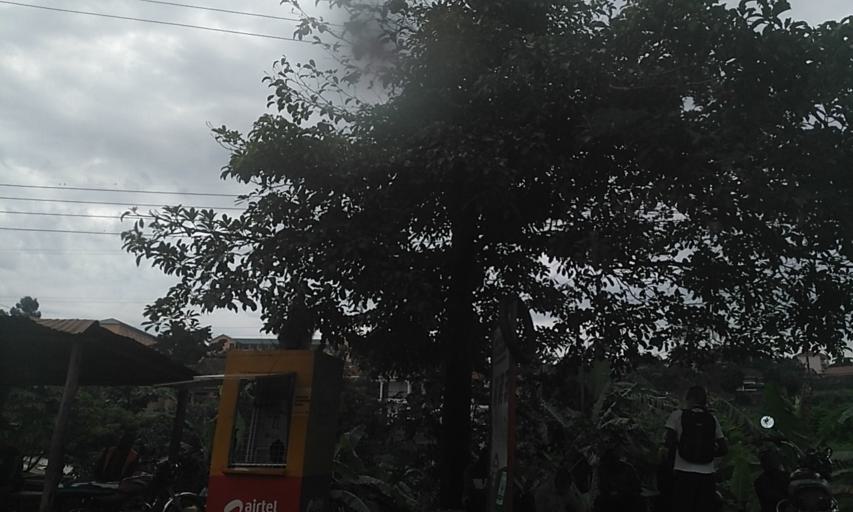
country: UG
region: Central Region
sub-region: Wakiso District
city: Kireka
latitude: 0.3637
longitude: 32.6353
